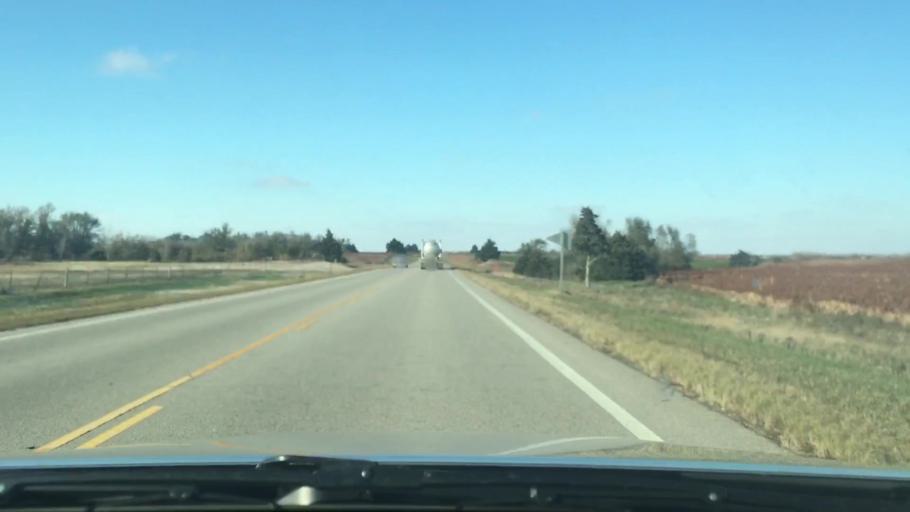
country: US
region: Kansas
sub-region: Rice County
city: Sterling
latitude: 38.1478
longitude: -98.2034
